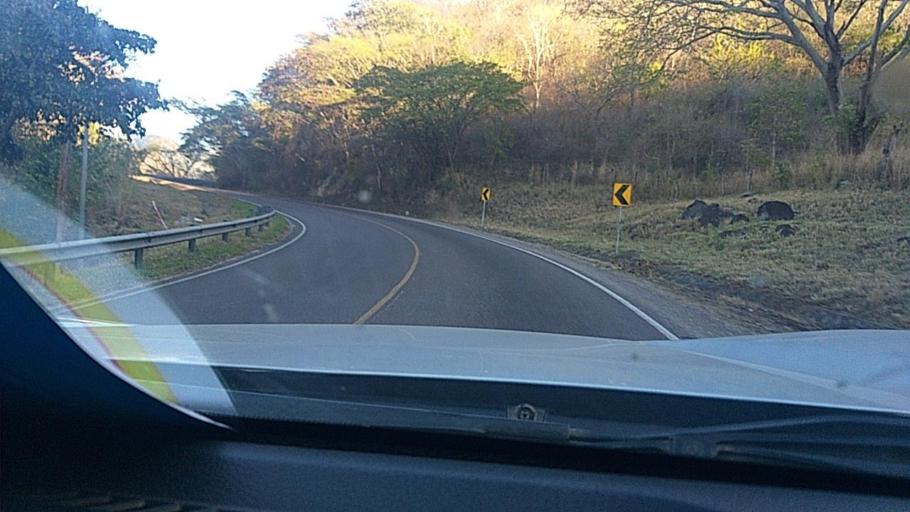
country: NI
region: Esteli
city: Condega
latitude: 13.2573
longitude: -86.3540
